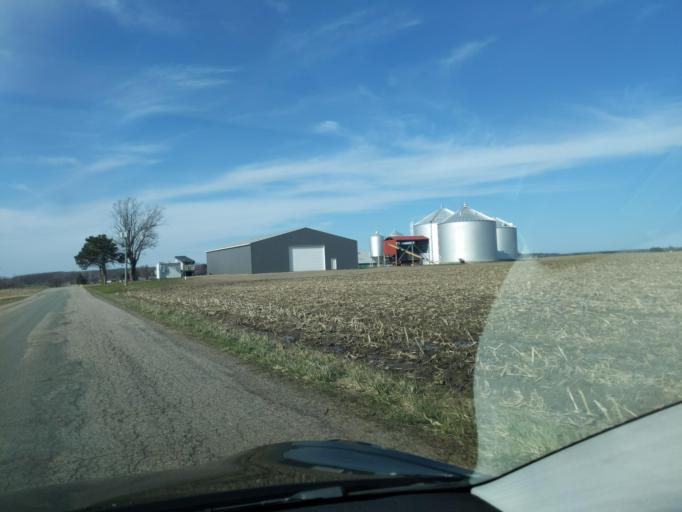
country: US
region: Michigan
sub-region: Ingham County
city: Williamston
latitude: 42.6090
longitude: -84.2993
